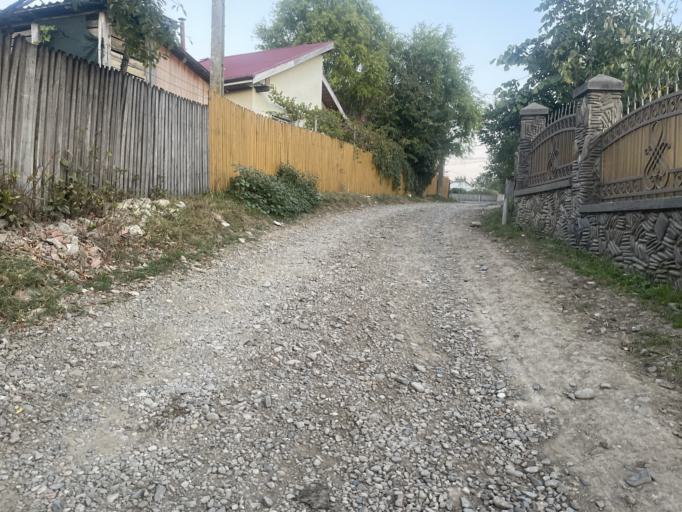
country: RO
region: Iasi
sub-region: Comuna Dumesti
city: Pausesti
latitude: 47.1543
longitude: 27.3217
